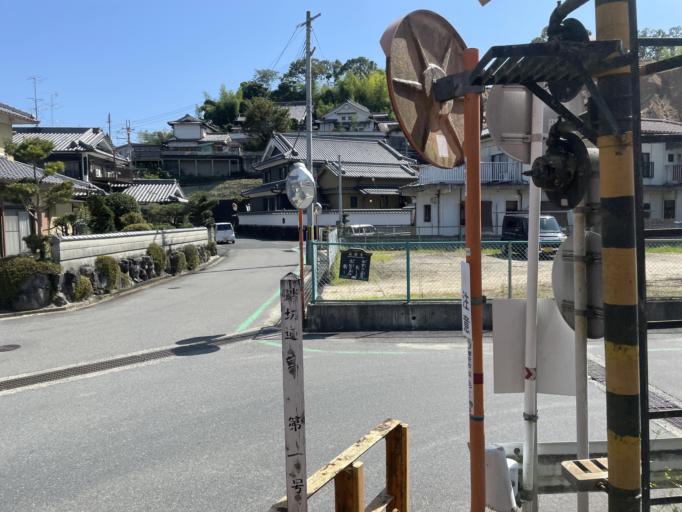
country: JP
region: Nara
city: Gose
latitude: 34.4303
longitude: 135.7589
